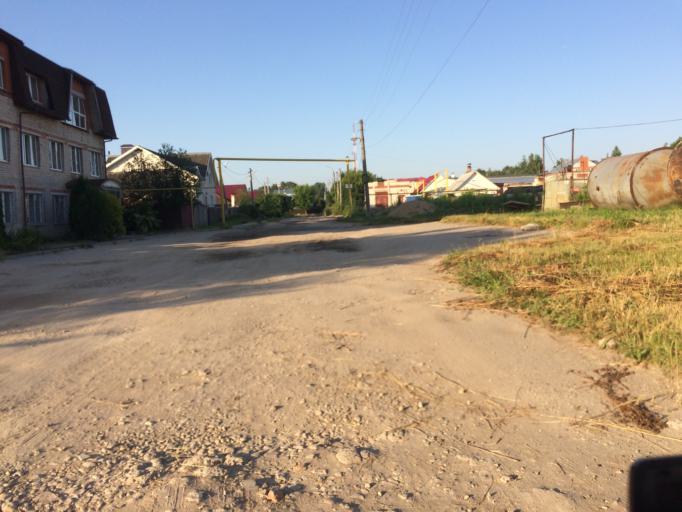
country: RU
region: Mariy-El
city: Yoshkar-Ola
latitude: 56.6558
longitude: 47.8876
